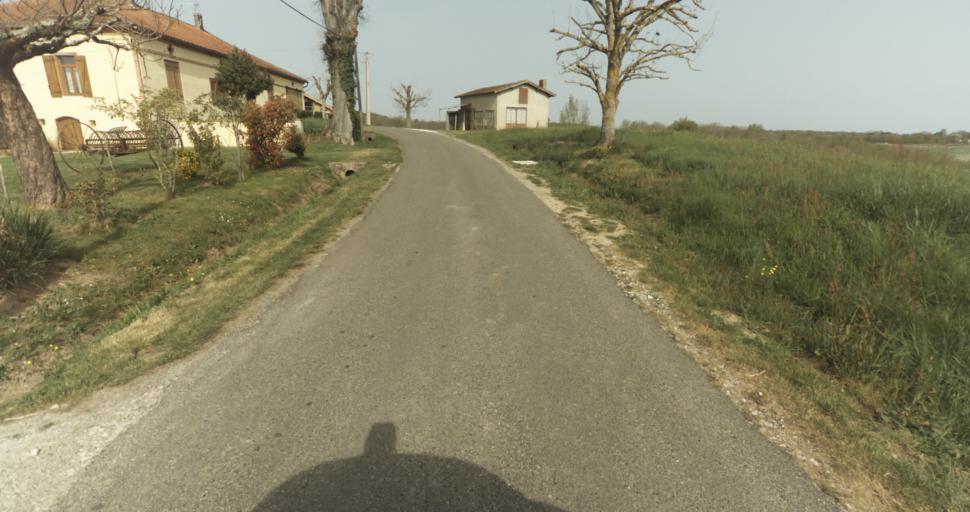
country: FR
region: Midi-Pyrenees
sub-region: Departement du Tarn-et-Garonne
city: Moissac
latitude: 44.1468
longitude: 1.0798
